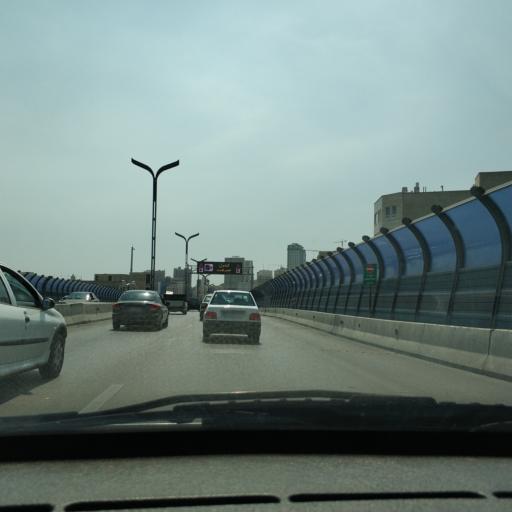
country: IR
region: Tehran
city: Tajrish
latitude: 35.7853
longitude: 51.4419
